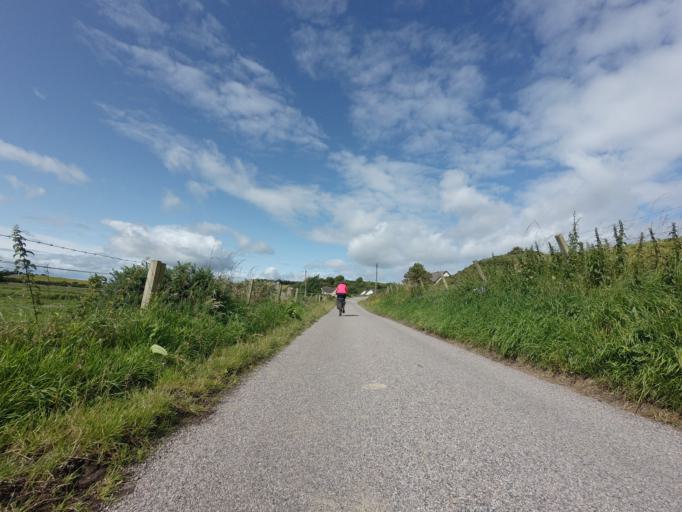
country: GB
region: Scotland
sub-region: Moray
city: Burghead
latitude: 57.6519
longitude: -3.4983
